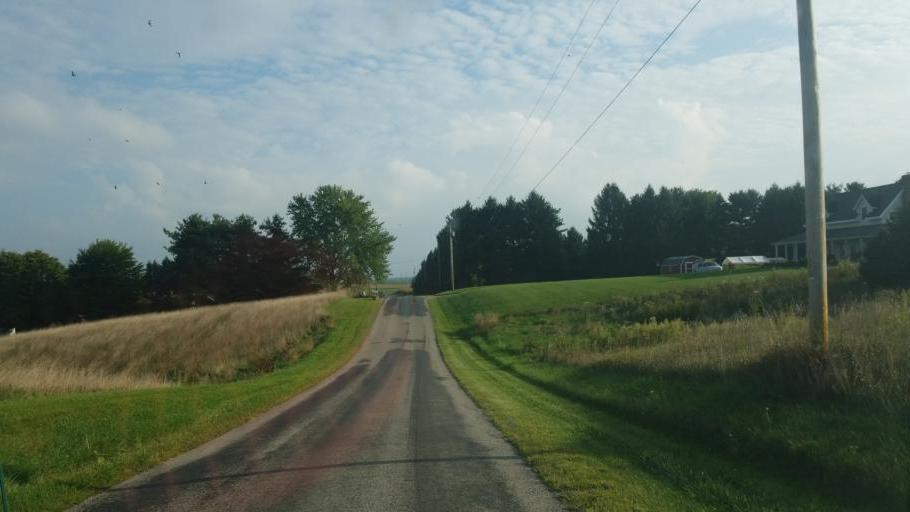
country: US
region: Ohio
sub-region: Wayne County
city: Wooster
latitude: 40.8885
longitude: -82.0223
